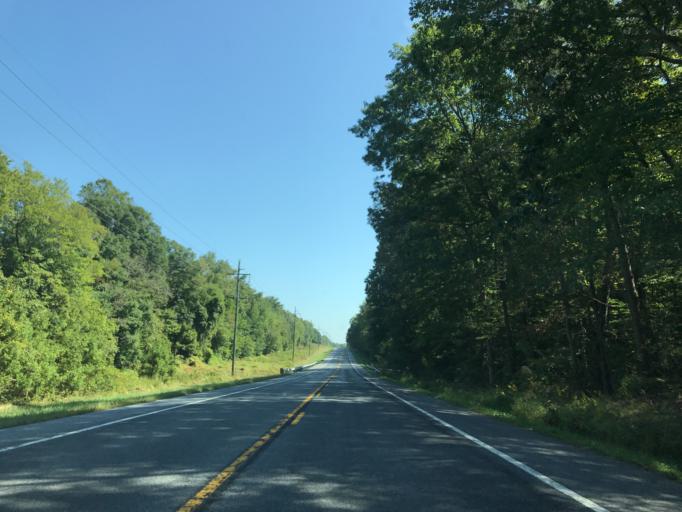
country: US
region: Maryland
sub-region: Queen Anne's County
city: Kingstown
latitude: 39.2643
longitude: -75.8833
